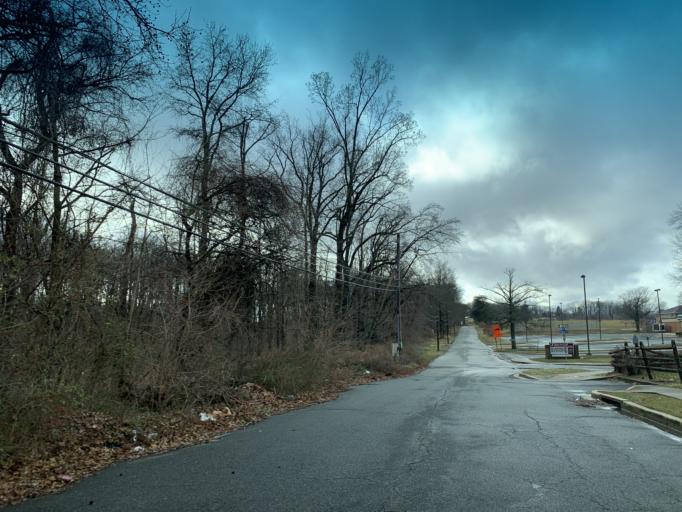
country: US
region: Maryland
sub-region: Harford County
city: Edgewood
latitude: 39.4234
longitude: -76.2972
